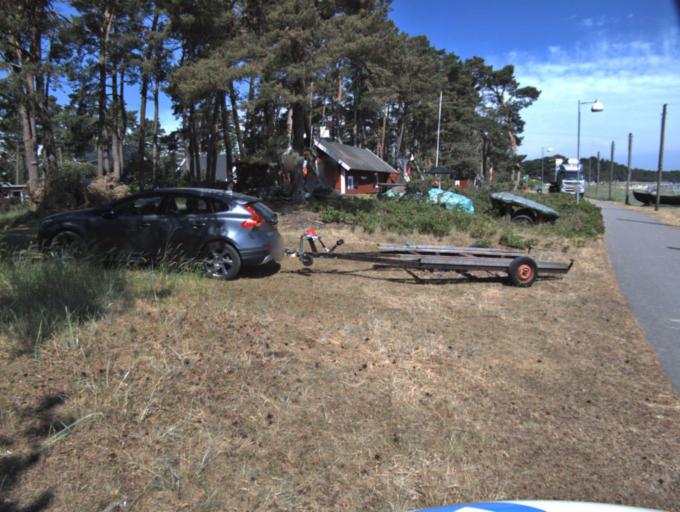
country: SE
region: Skane
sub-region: Kristianstads Kommun
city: Ahus
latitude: 55.9340
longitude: 14.3200
